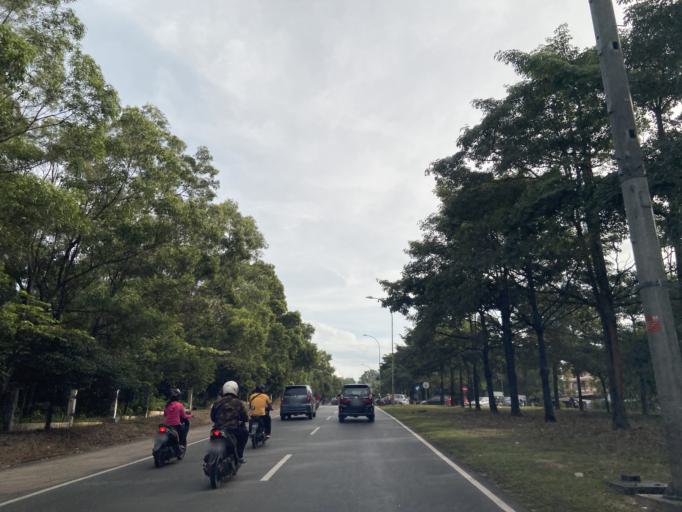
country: SG
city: Singapore
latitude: 1.1374
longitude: 104.0231
